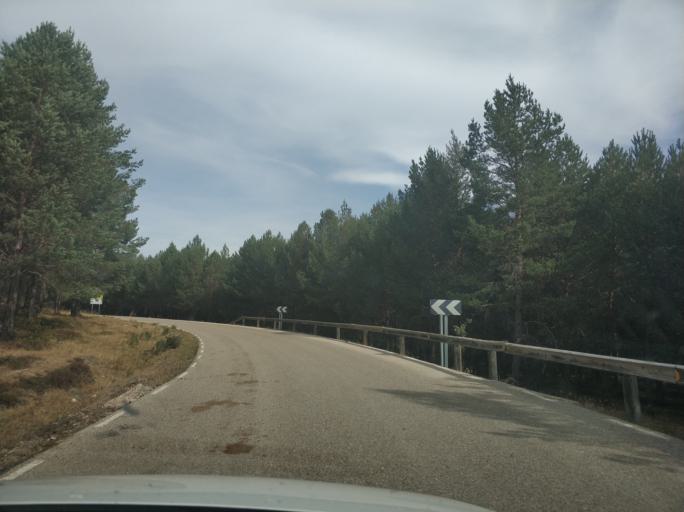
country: ES
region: Castille and Leon
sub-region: Provincia de Soria
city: Duruelo de la Sierra
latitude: 41.8775
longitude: -2.9373
